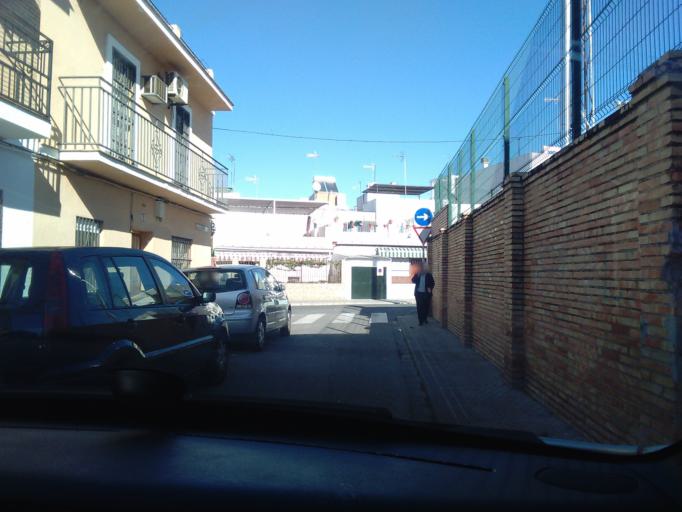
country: ES
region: Andalusia
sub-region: Provincia de Sevilla
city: Sevilla
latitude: 37.3851
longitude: -5.9064
